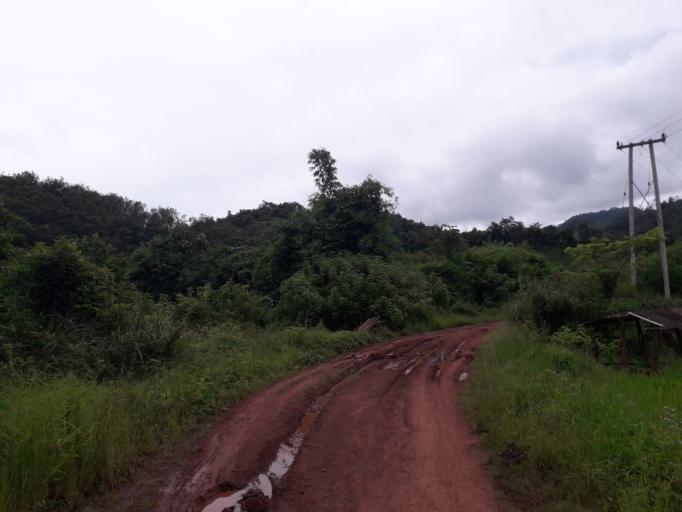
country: CN
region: Yunnan
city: Menglie
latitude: 22.2115
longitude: 101.6603
